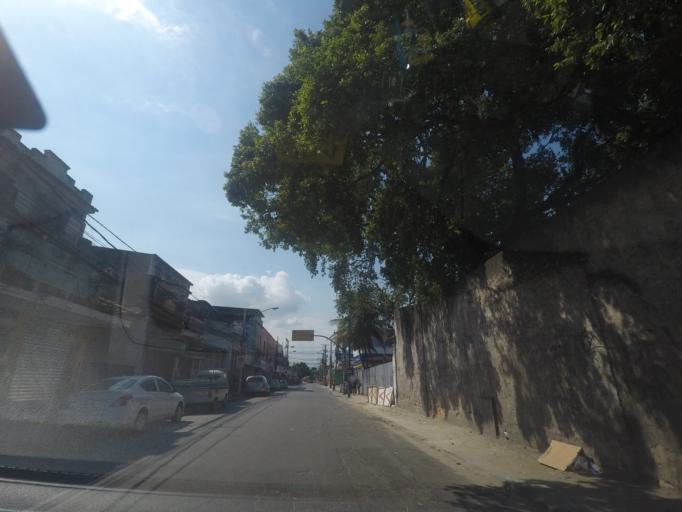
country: BR
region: Rio de Janeiro
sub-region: Rio De Janeiro
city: Rio de Janeiro
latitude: -22.8996
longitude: -43.2166
